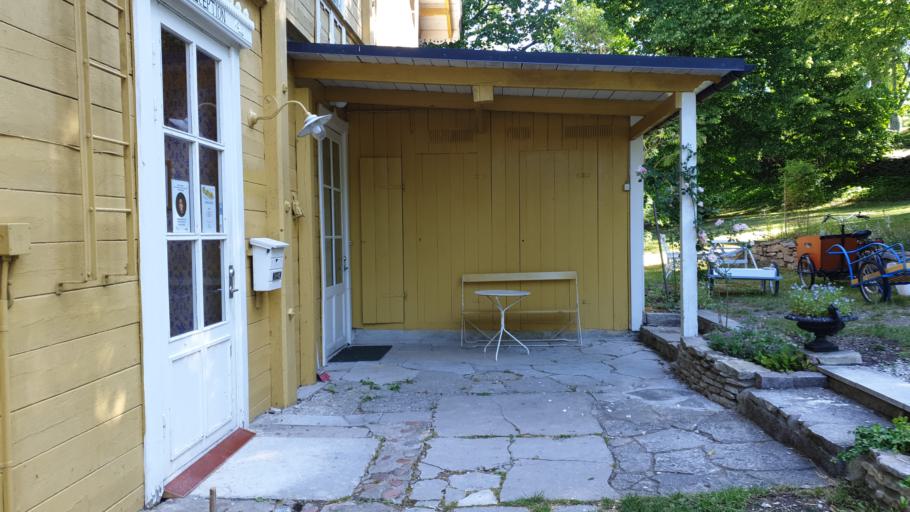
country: SE
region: Gotland
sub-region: Gotland
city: Vibble
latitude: 57.6001
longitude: 18.2168
